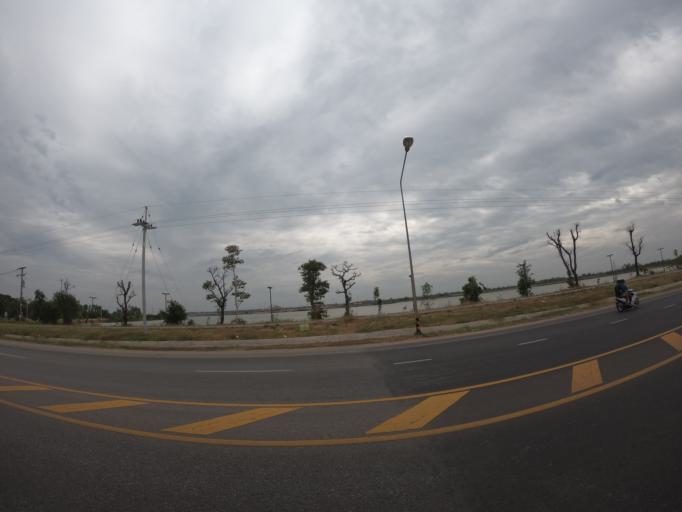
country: TH
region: Roi Et
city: Thawat Buri
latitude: 16.0827
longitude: 103.7200
